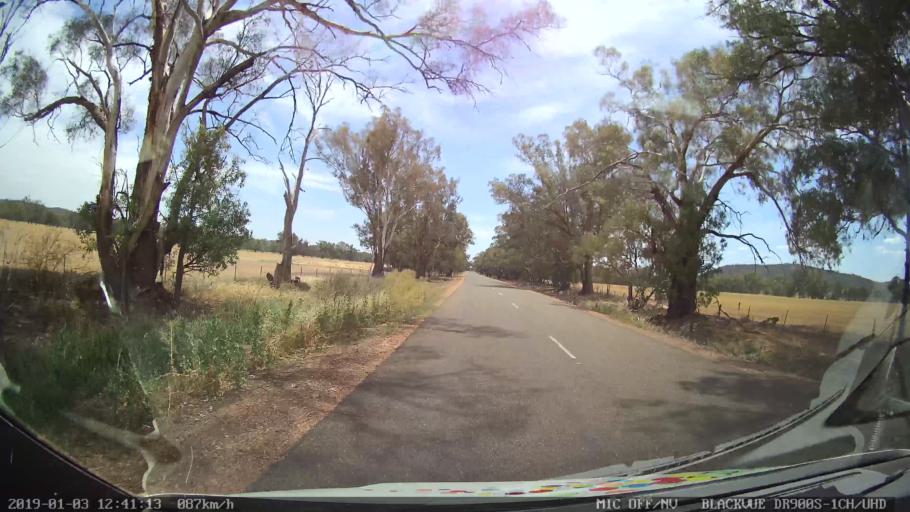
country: AU
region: New South Wales
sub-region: Weddin
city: Grenfell
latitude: -33.8025
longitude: 148.2147
